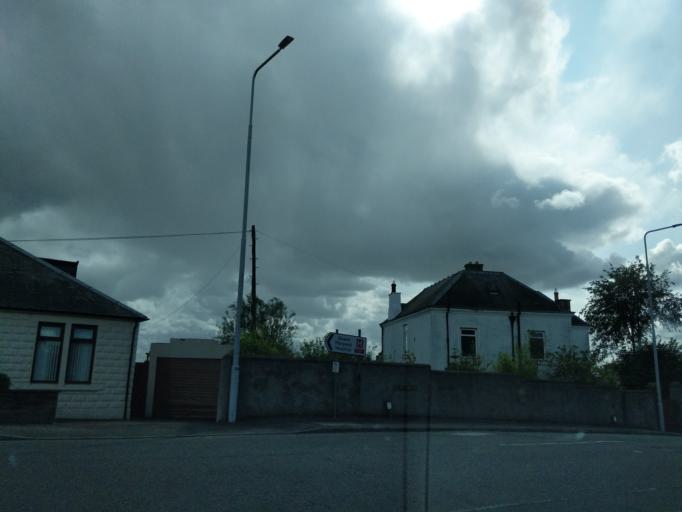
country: GB
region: Scotland
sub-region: Fife
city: Townhill
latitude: 56.0832
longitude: -3.4459
